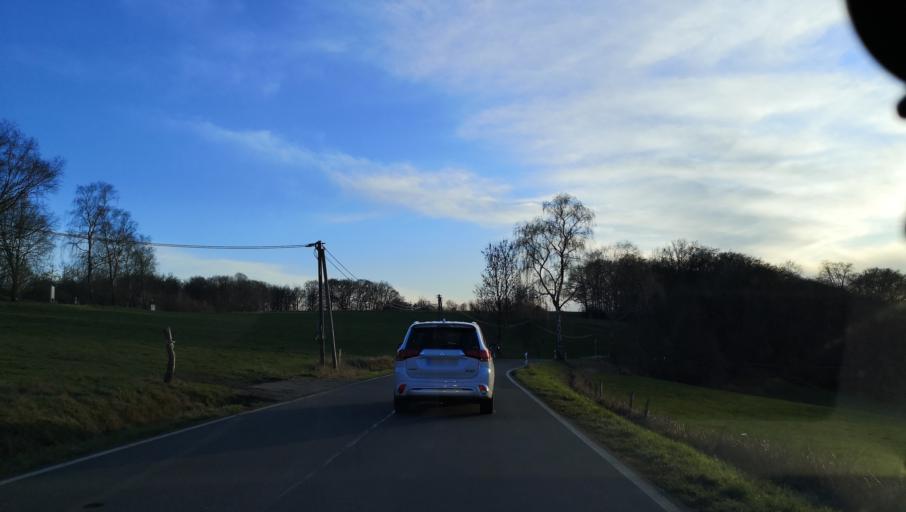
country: DE
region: North Rhine-Westphalia
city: Wipperfurth
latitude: 51.1514
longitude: 7.3902
